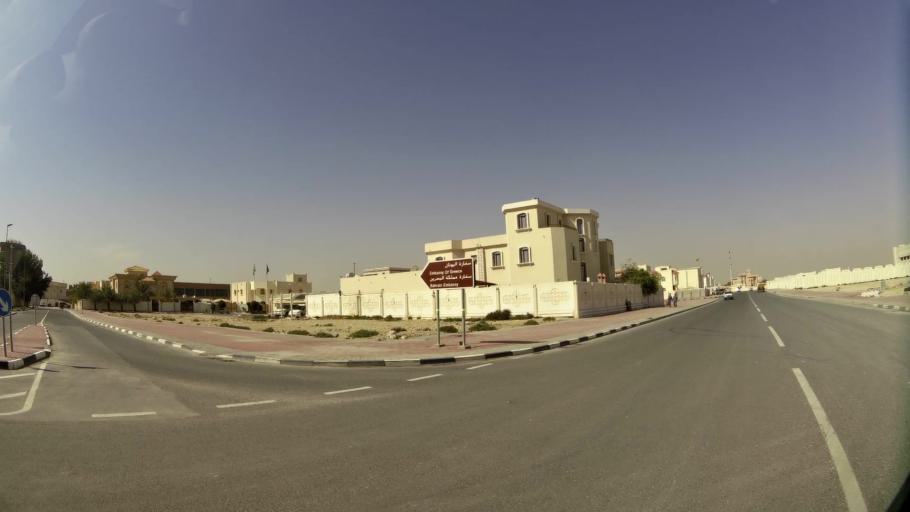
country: QA
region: Baladiyat ad Dawhah
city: Doha
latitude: 25.3560
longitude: 51.5139
